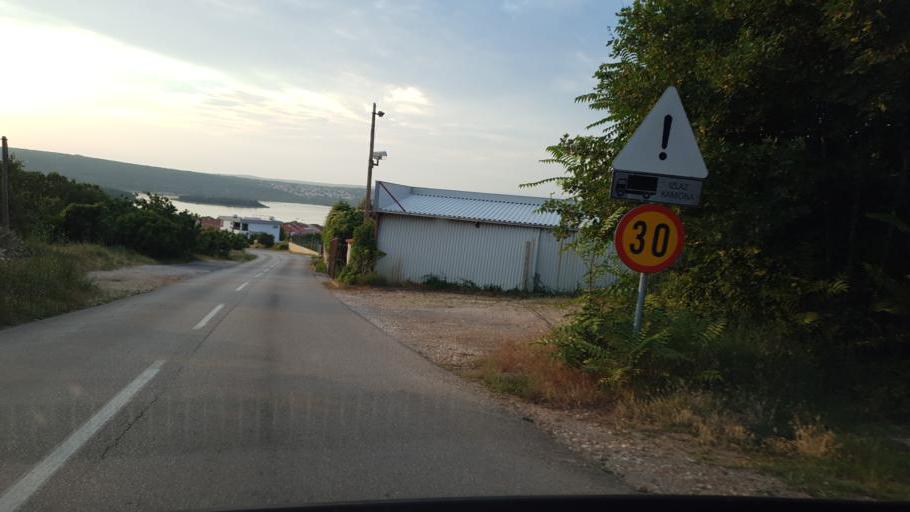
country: HR
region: Primorsko-Goranska
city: Punat
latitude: 45.0080
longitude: 14.6322
